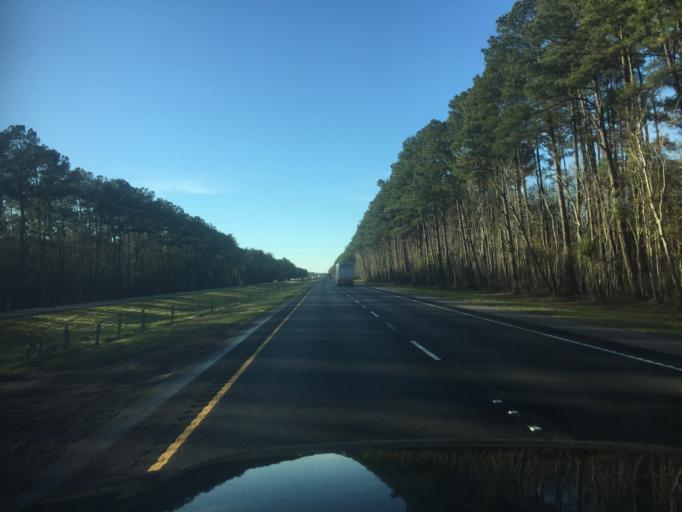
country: US
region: Louisiana
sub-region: Saint Tammany Parish
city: Lacombe
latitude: 30.3837
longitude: -89.9824
